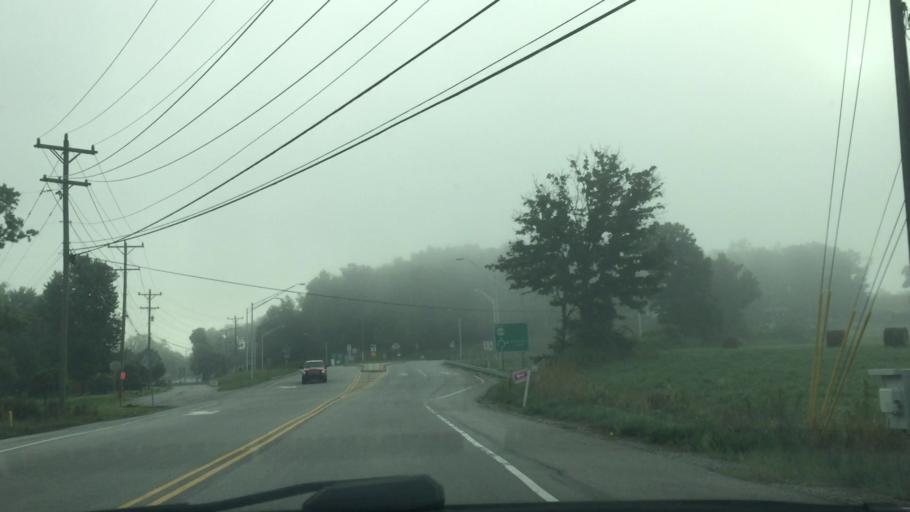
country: US
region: Pennsylvania
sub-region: Washington County
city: Canonsburg
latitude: 40.2028
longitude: -80.1279
